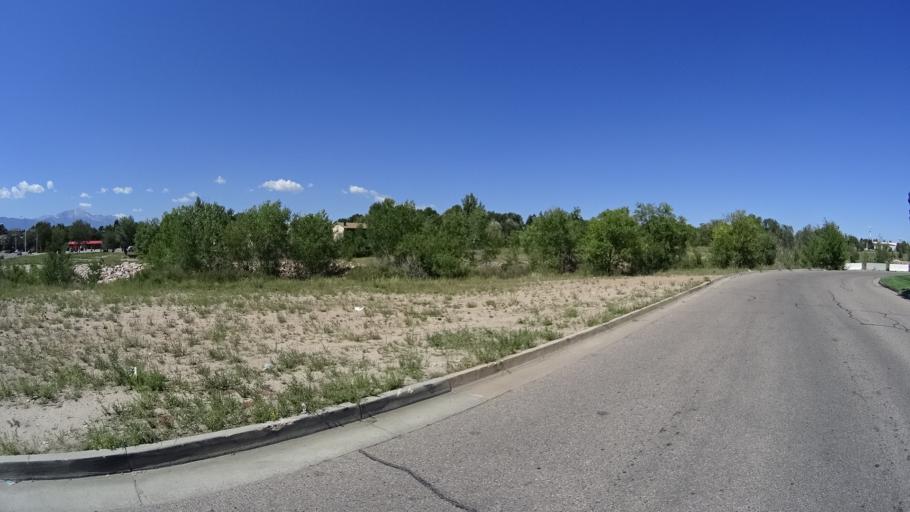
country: US
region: Colorado
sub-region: El Paso County
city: Cimarron Hills
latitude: 38.8576
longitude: -104.7230
